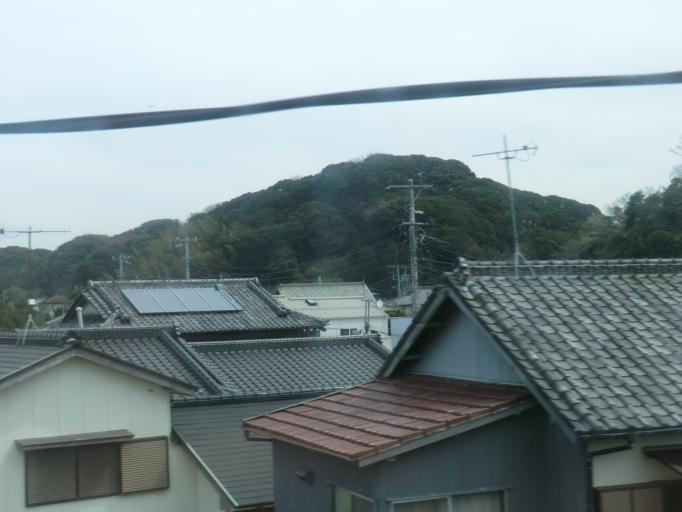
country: JP
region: Chiba
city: Futtsu
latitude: 35.2850
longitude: 139.8574
